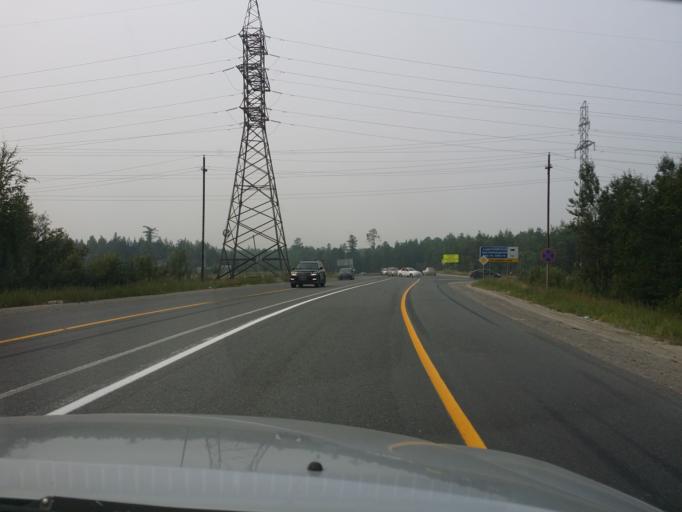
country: RU
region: Khanty-Mansiyskiy Avtonomnyy Okrug
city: Nizhnevartovsk
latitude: 60.9759
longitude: 76.5578
